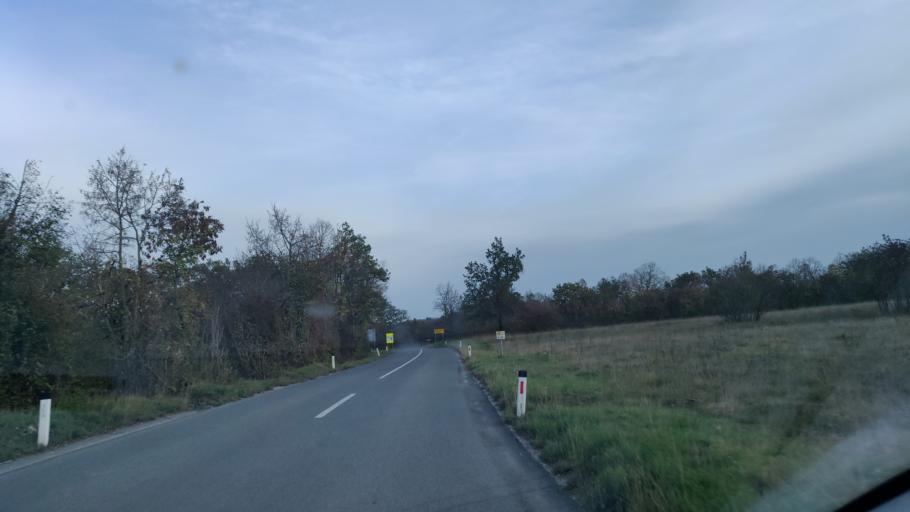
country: SI
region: Komen
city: Komen
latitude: 45.8134
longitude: 13.7948
